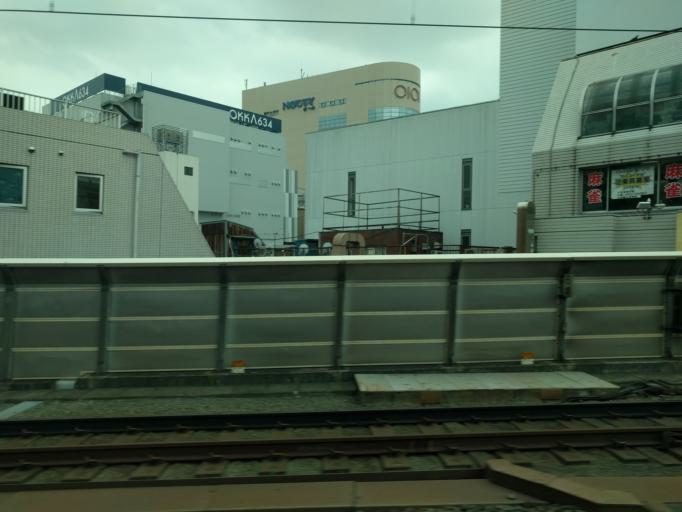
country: JP
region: Tokyo
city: Chofugaoka
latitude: 35.6004
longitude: 139.6117
